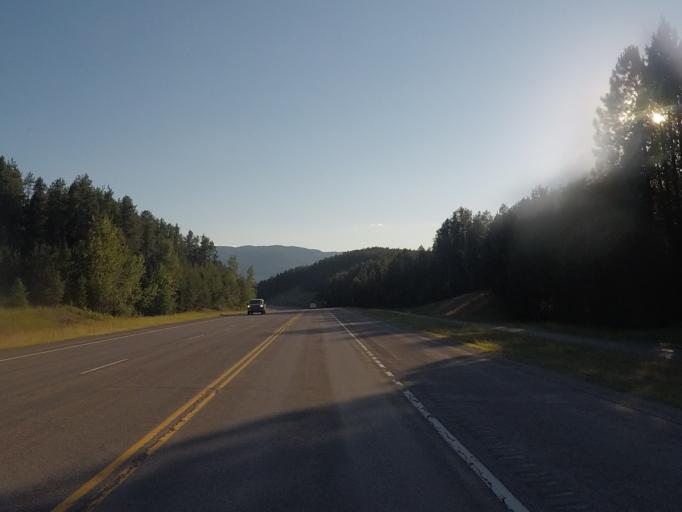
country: US
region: Montana
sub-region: Flathead County
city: Columbia Falls
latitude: 48.4514
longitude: -114.0212
